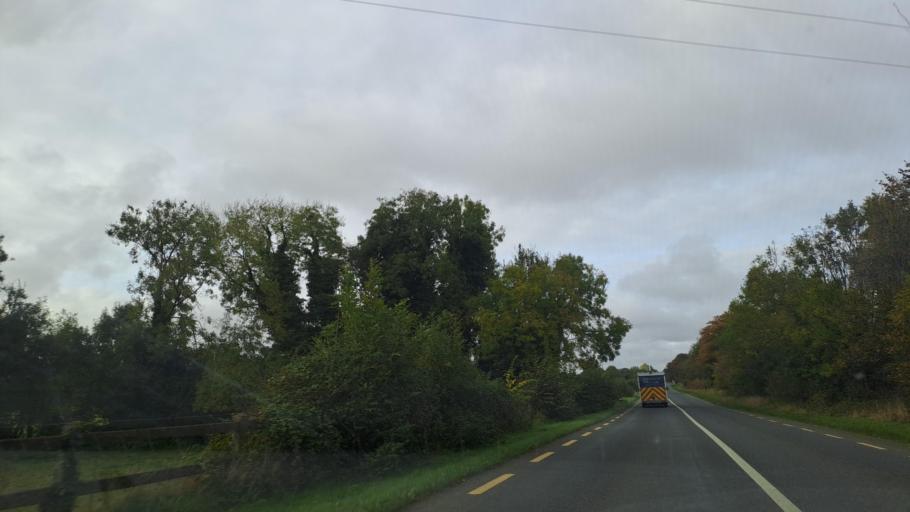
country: IE
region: Leinster
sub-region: An Mhi
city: Navan
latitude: 53.7599
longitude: -6.7249
